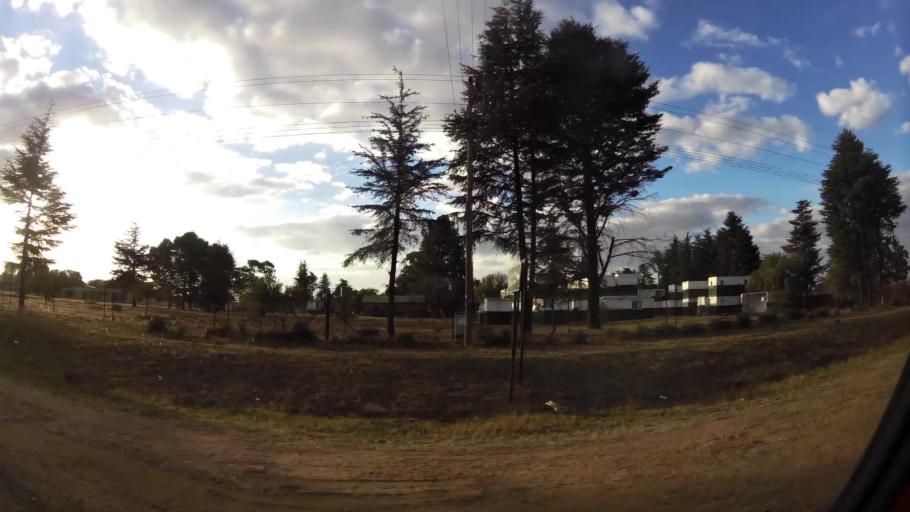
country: ZA
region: Gauteng
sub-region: City of Johannesburg Metropolitan Municipality
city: Midrand
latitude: -25.9581
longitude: 28.1591
